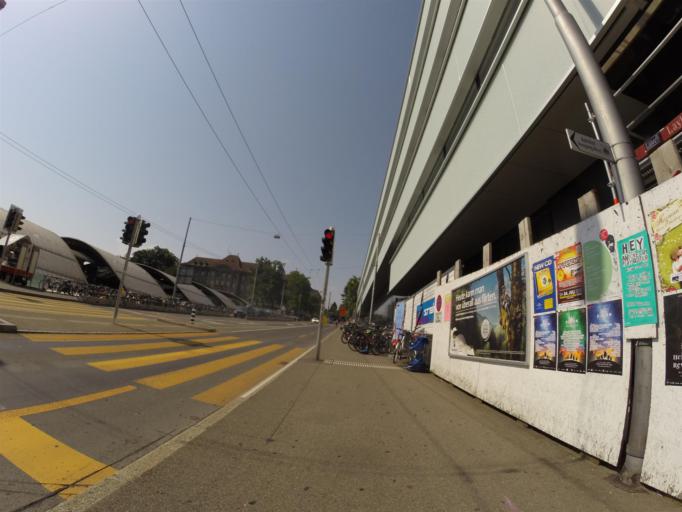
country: CH
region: Bern
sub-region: Bern-Mittelland District
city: Bern
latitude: 46.9481
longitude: 7.4371
